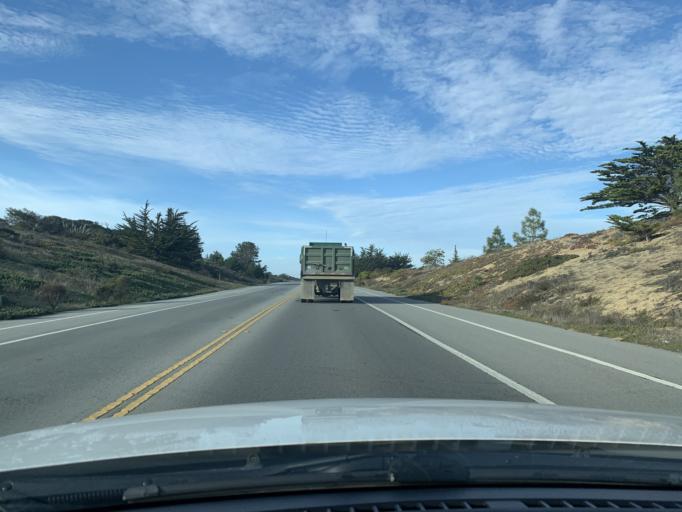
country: US
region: California
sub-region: Monterey County
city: Marina
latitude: 36.6634
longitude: -121.7816
